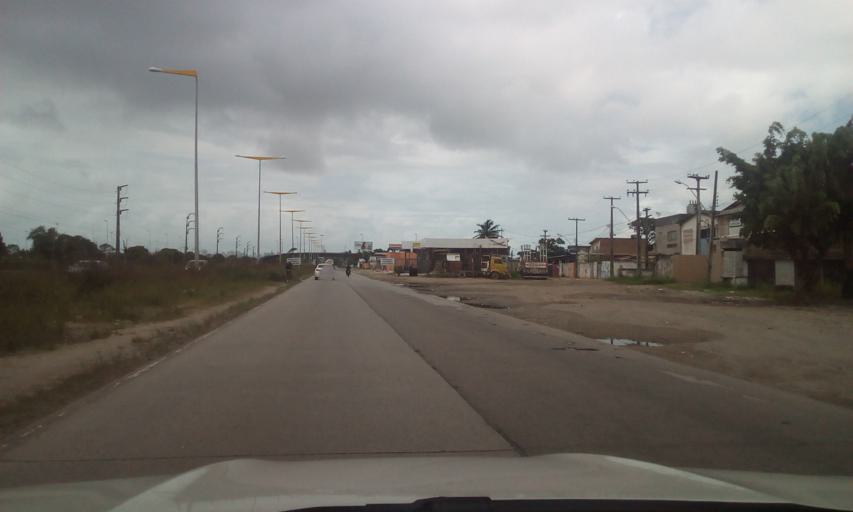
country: BR
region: Pernambuco
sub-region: Recife
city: Recife
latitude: -8.0713
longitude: -34.9392
